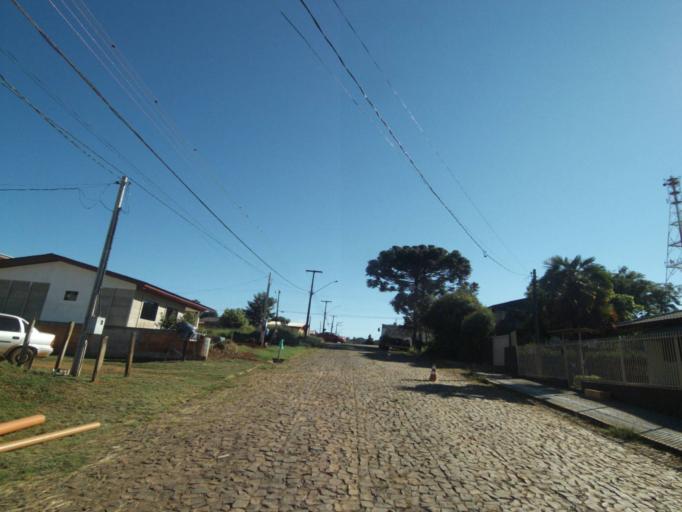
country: BR
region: Parana
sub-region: Pinhao
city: Pinhao
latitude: -25.8396
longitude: -52.0291
